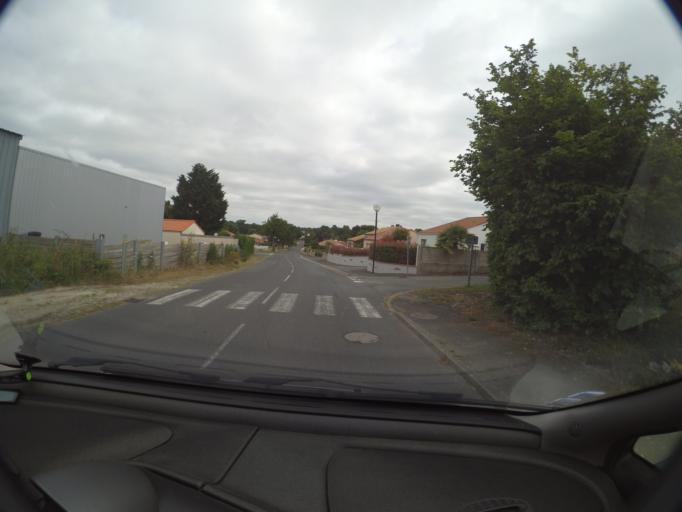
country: FR
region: Pays de la Loire
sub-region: Departement de la Vendee
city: Saint-Hilaire-de-Loulay
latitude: 47.0014
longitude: -1.3384
